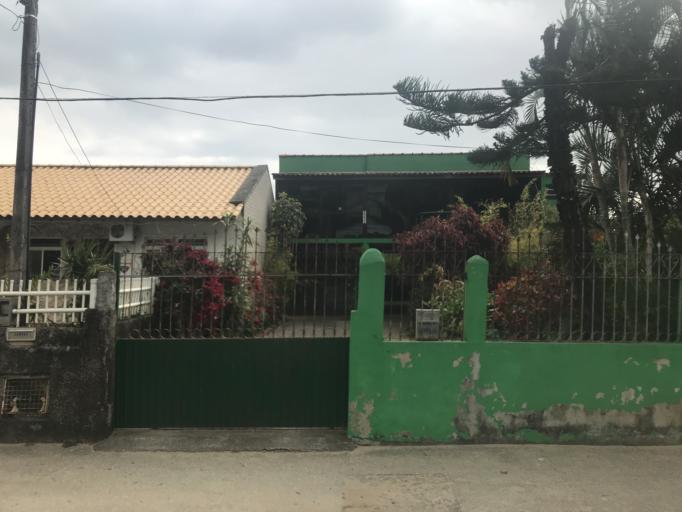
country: BR
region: Santa Catarina
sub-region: Florianopolis
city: Costeira do Pirajubae
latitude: -27.6385
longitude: -48.5221
